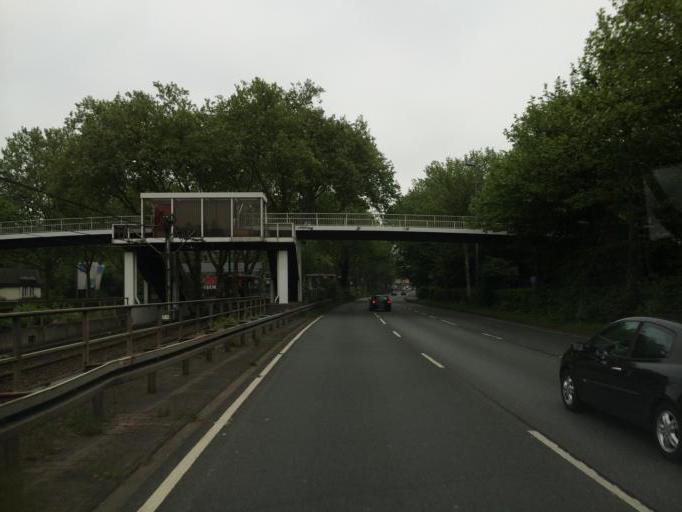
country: DE
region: North Rhine-Westphalia
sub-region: Regierungsbezirk Arnsberg
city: Dortmund
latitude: 51.5023
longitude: 7.4904
